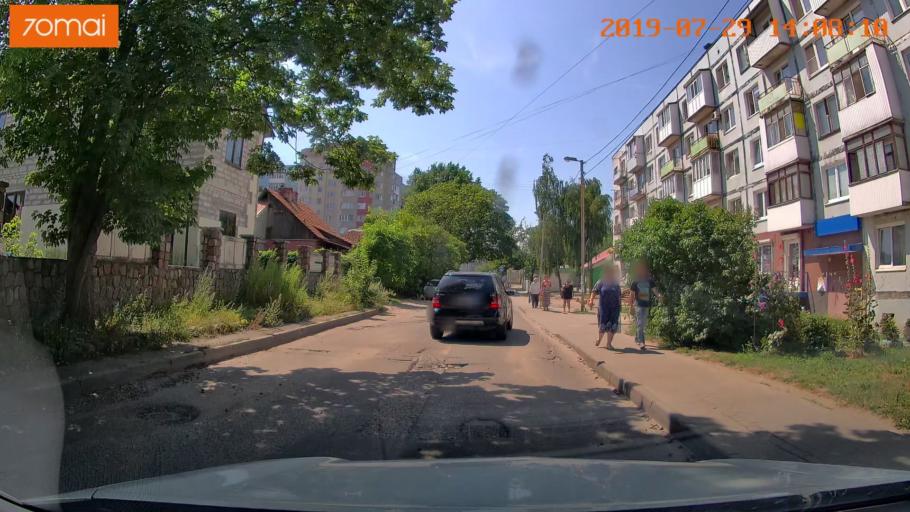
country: RU
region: Kaliningrad
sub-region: Gorod Kaliningrad
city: Baltiysk
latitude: 54.6575
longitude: 19.9081
